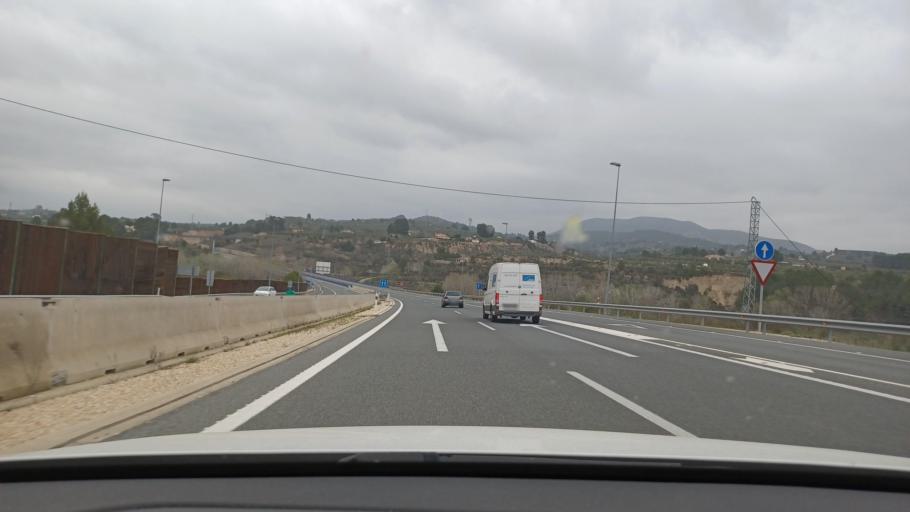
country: ES
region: Valencia
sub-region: Provincia de Alicante
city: Cocentaina
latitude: 38.7370
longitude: -0.4257
